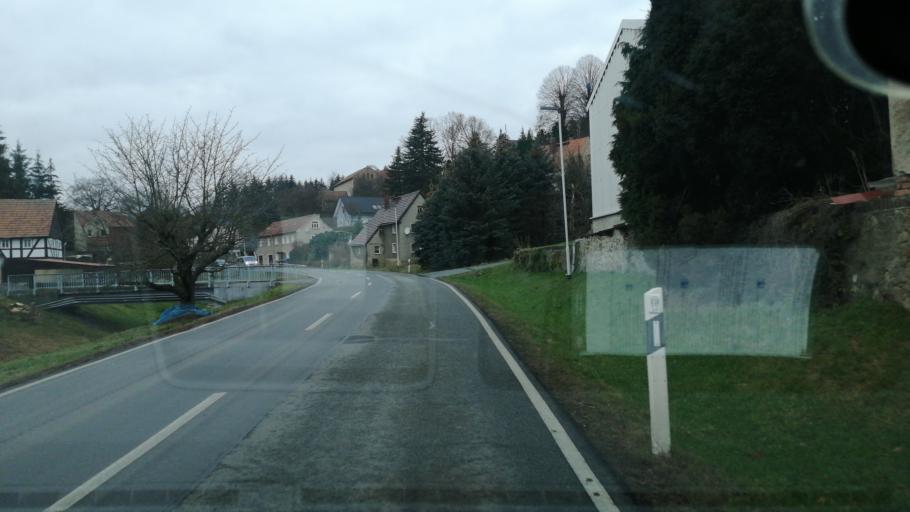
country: DE
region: Saxony
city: Bernstadt
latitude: 51.0632
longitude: 14.8048
